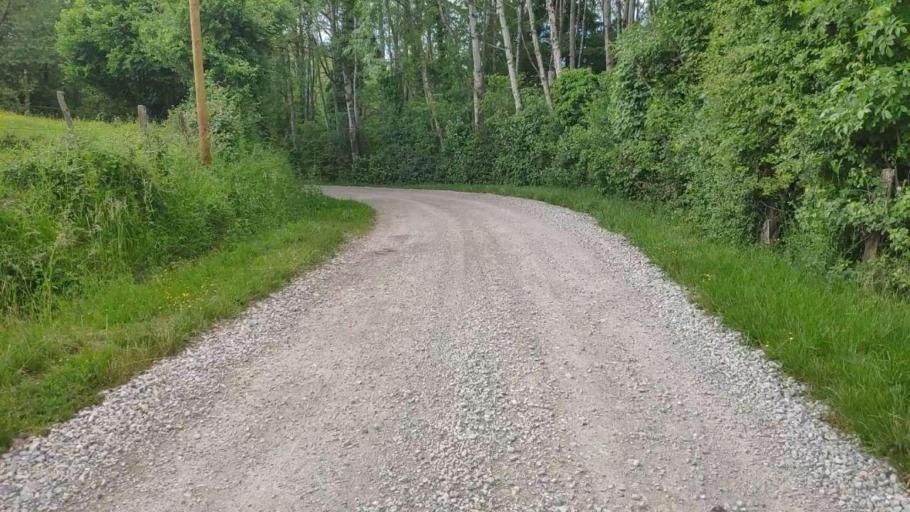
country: FR
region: Franche-Comte
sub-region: Departement du Jura
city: Montmorot
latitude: 46.7510
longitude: 5.5520
